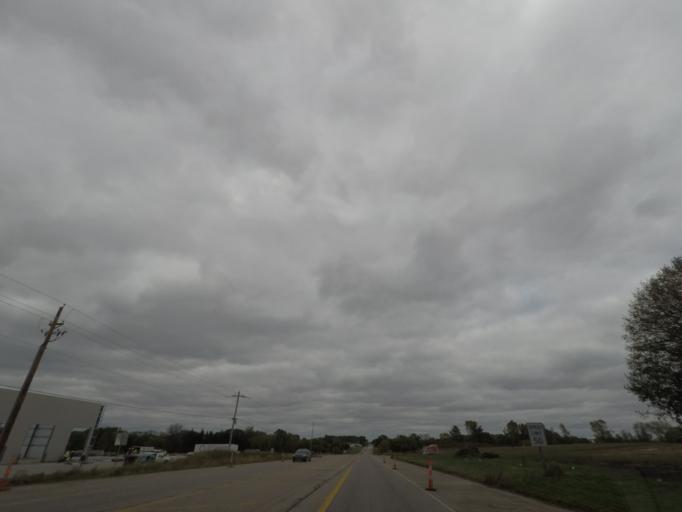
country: US
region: Iowa
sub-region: Polk County
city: Saylorville
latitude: 41.6817
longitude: -93.6005
